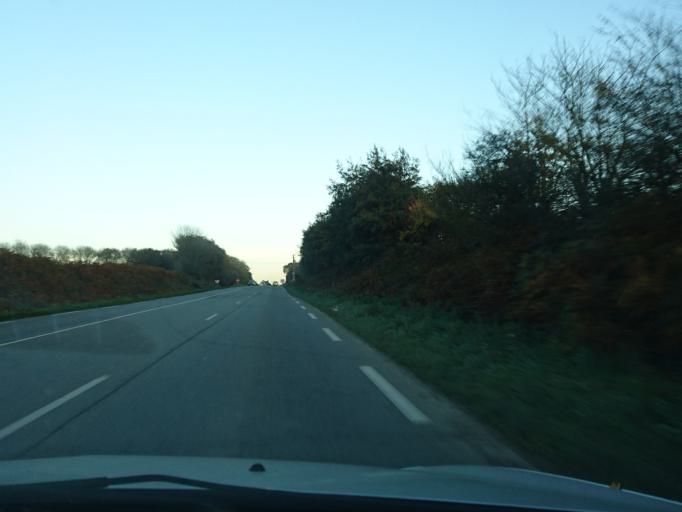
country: FR
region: Brittany
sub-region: Departement du Finistere
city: Guilers
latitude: 48.4277
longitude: -4.5845
